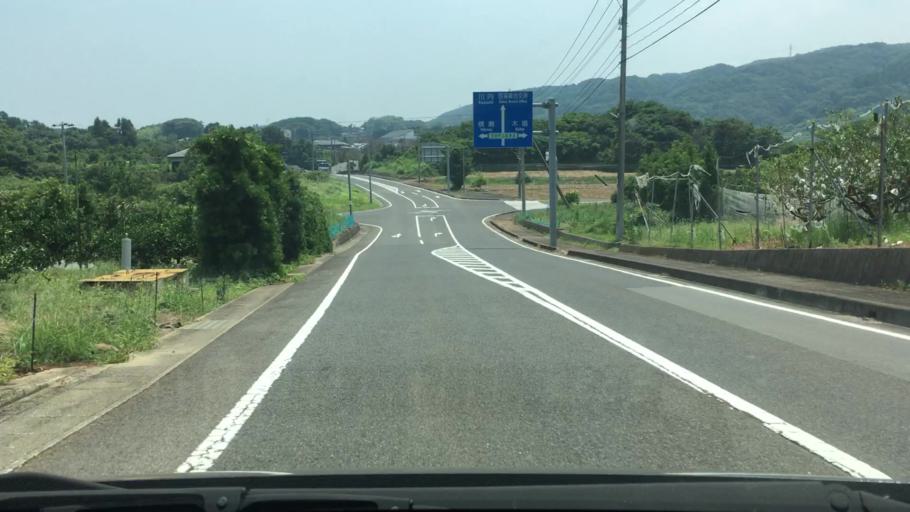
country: JP
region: Nagasaki
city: Sasebo
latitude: 33.0676
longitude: 129.6823
